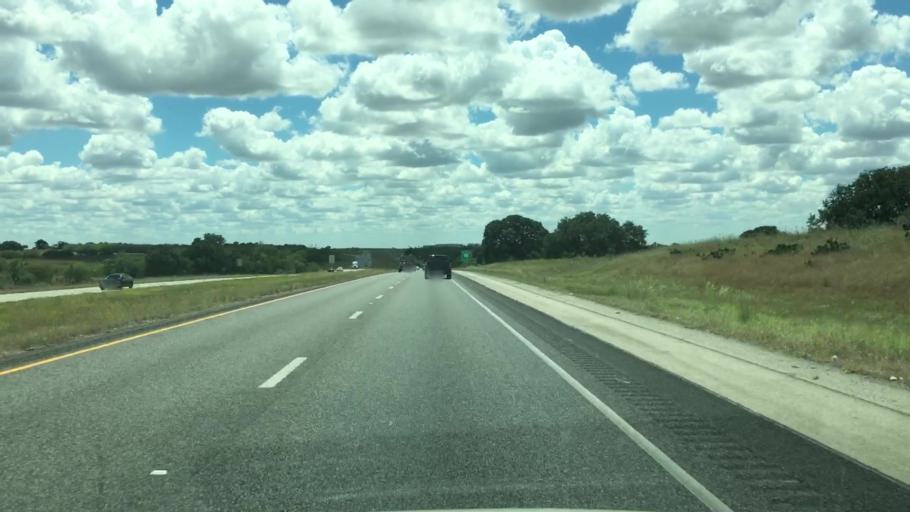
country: US
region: Texas
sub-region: Atascosa County
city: Poteet
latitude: 29.1192
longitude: -98.4317
